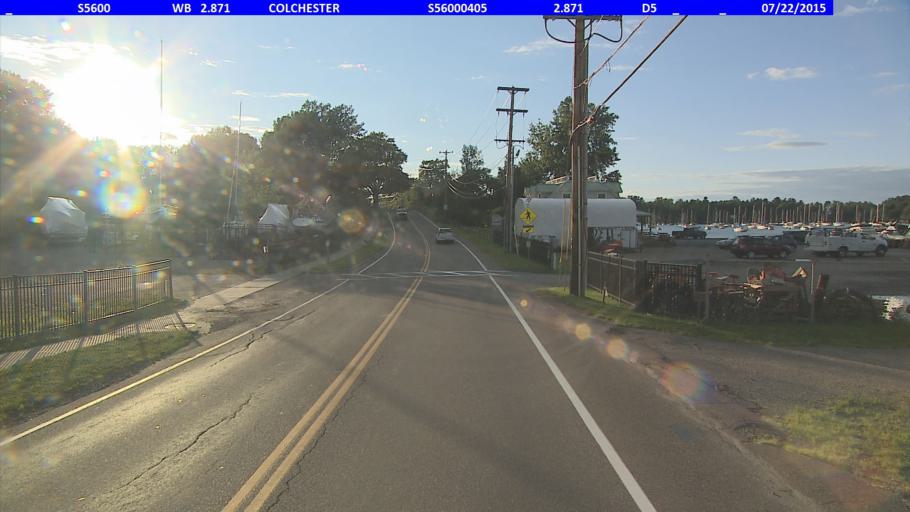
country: US
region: Vermont
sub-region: Chittenden County
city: Winooski
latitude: 44.5474
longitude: -73.2213
